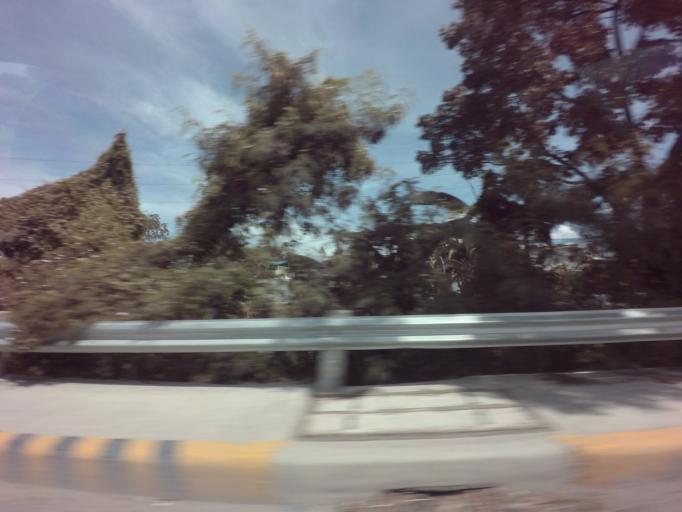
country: PH
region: Calabarzon
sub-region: Province of Rizal
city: Taguig
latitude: 14.5106
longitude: 121.0711
